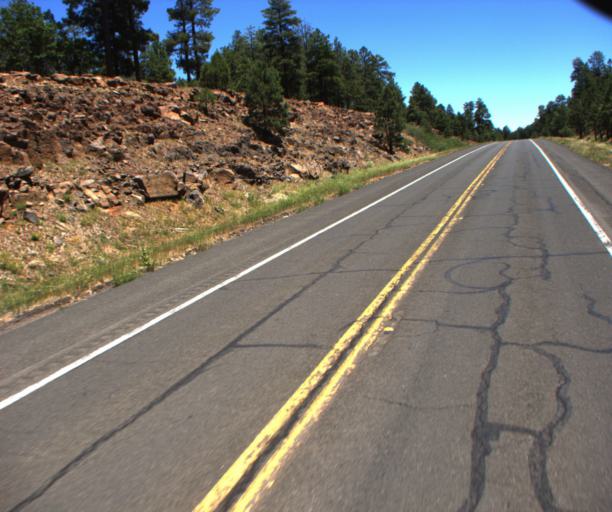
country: US
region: Arizona
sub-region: Gila County
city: Pine
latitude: 34.5525
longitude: -111.2984
